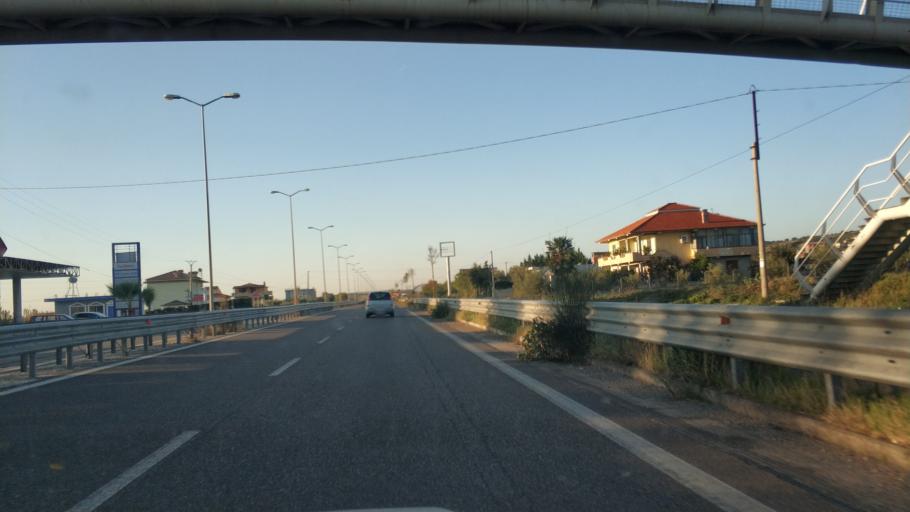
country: AL
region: Tirane
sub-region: Rrethi i Kavajes
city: Lekaj
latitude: 41.1102
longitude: 19.6068
